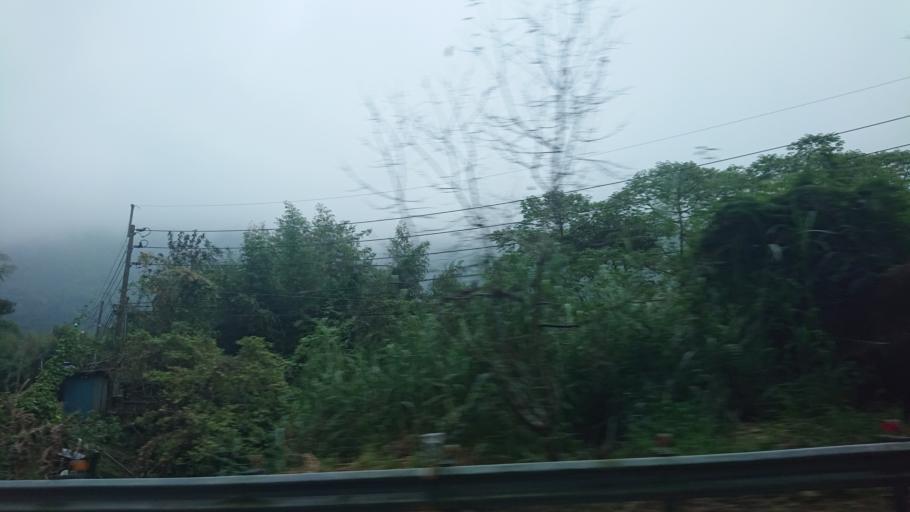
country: TW
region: Taiwan
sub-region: Chiayi
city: Jiayi Shi
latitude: 23.4762
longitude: 120.7123
